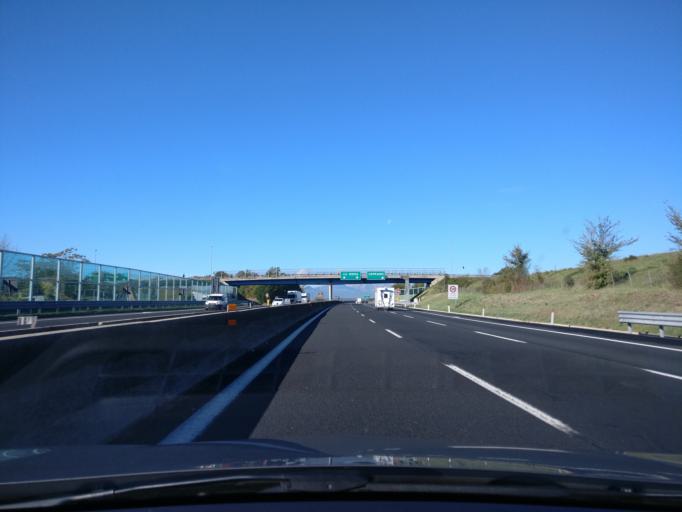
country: IT
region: Latium
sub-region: Provincia di Frosinone
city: Ceprano
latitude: 41.5432
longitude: 13.4969
